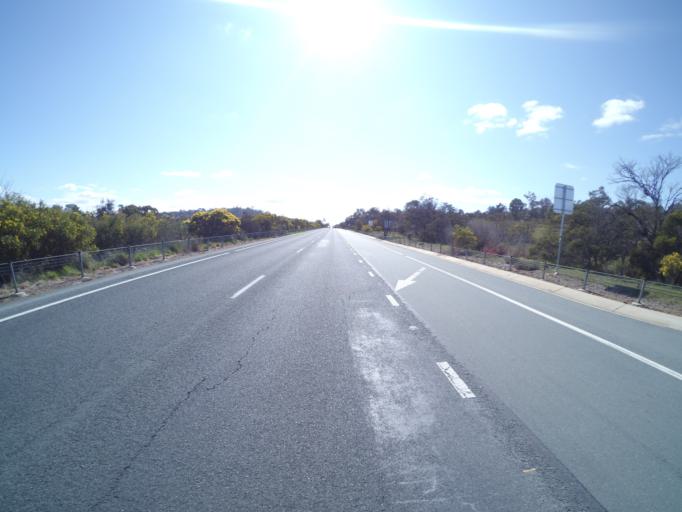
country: AU
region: Australian Capital Territory
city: Kaleen
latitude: -35.2189
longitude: 149.1807
